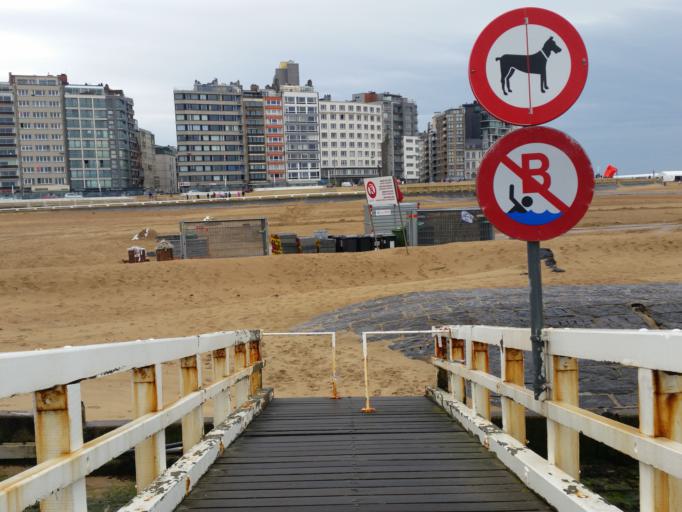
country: BE
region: Flanders
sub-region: Provincie West-Vlaanderen
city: Ostend
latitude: 51.2365
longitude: 2.9216
